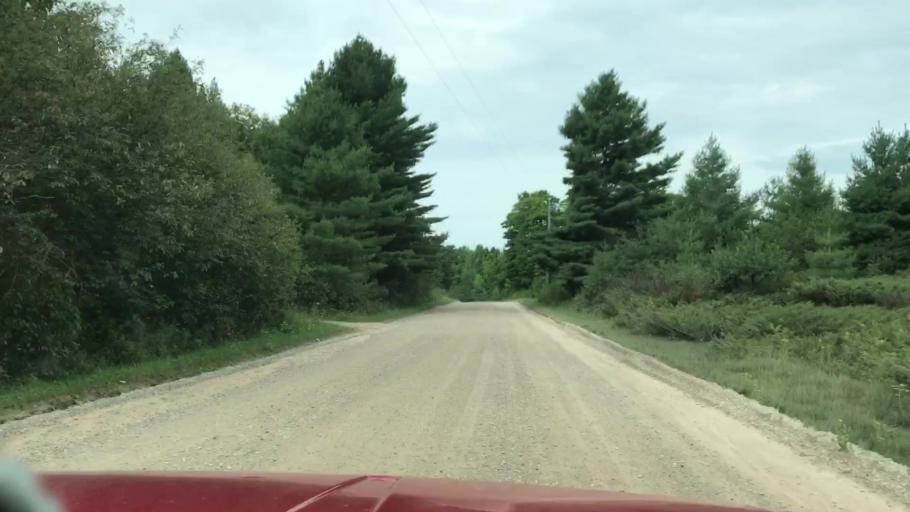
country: US
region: Michigan
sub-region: Charlevoix County
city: Charlevoix
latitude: 45.7285
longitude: -85.5449
